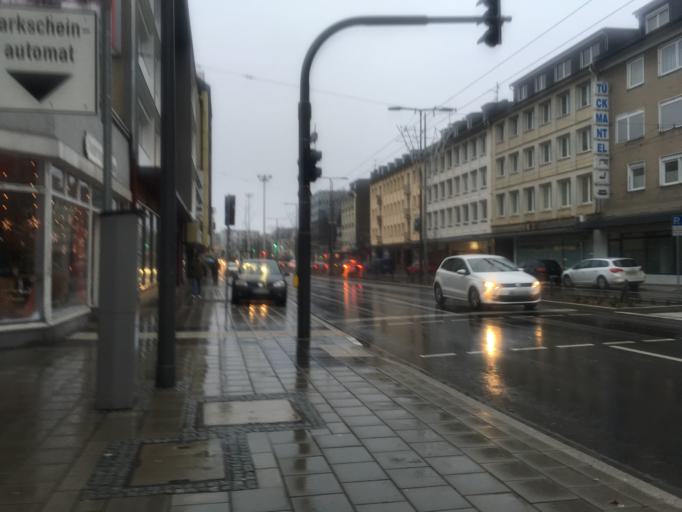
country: DE
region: North Rhine-Westphalia
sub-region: Regierungsbezirk Dusseldorf
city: Solingen
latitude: 51.1758
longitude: 7.0842
